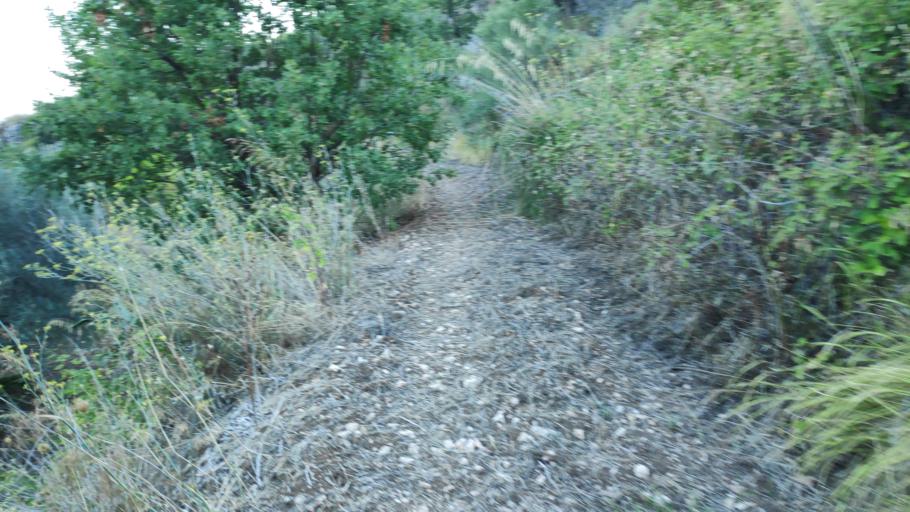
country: IT
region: Calabria
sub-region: Provincia di Reggio Calabria
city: Pazzano
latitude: 38.4649
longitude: 16.4482
